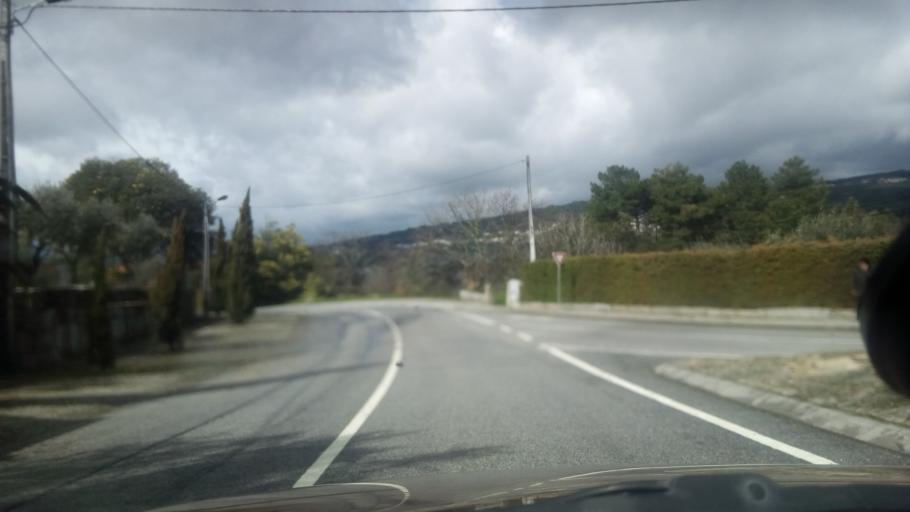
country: PT
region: Guarda
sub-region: Fornos de Algodres
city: Fornos de Algodres
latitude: 40.6061
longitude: -7.5110
